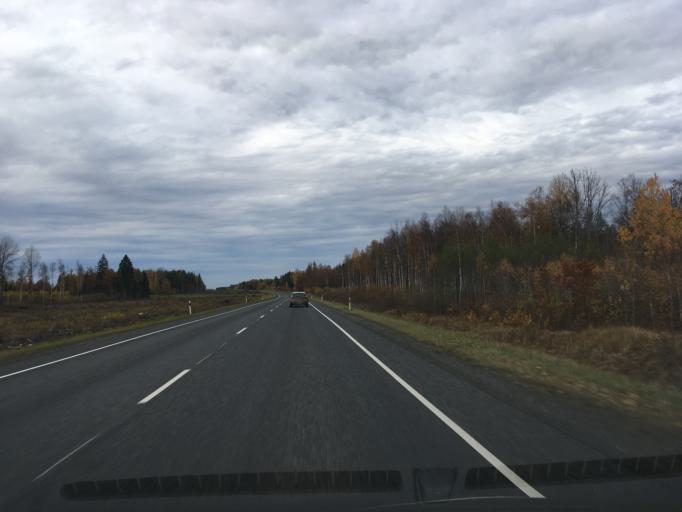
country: EE
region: Harju
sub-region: Nissi vald
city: Turba
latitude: 58.9463
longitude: 24.0849
